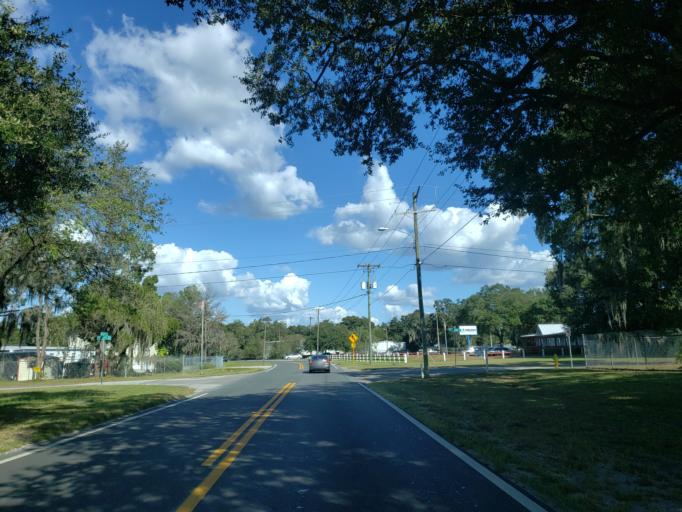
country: US
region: Florida
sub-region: Hillsborough County
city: Plant City
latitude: 28.0034
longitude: -82.1506
